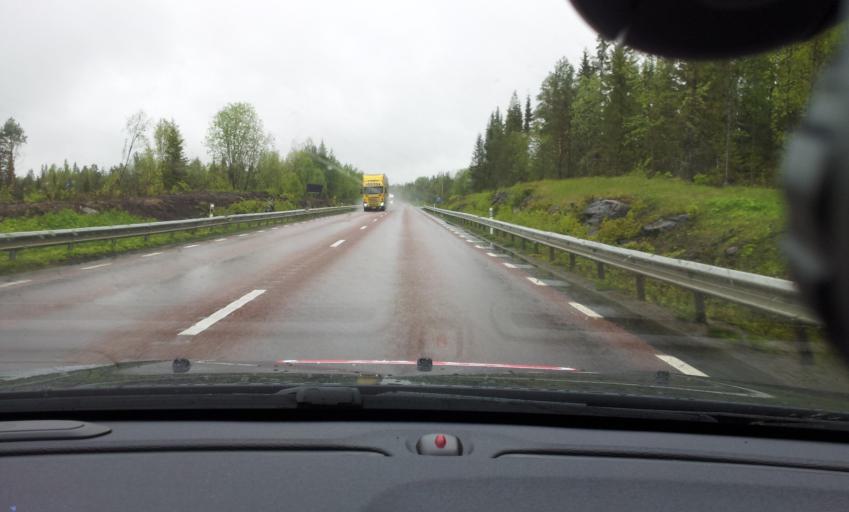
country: SE
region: Jaemtland
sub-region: Bergs Kommun
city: Hoverberg
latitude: 62.9342
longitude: 14.5397
